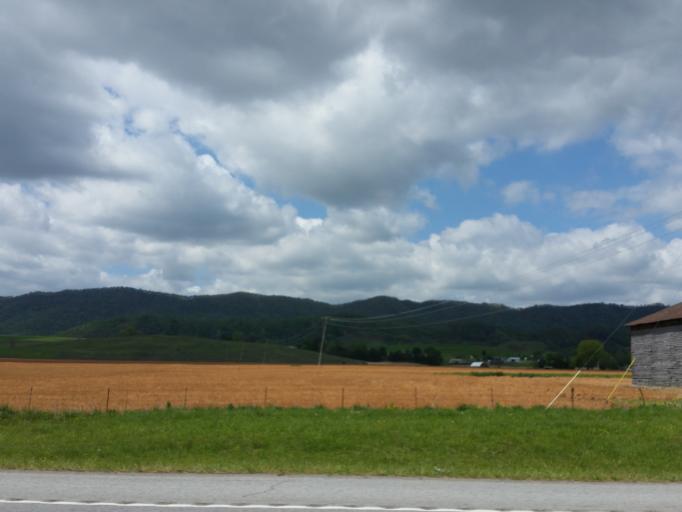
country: US
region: Kentucky
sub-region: Bell County
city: Middlesboro
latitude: 36.5221
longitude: -83.7540
